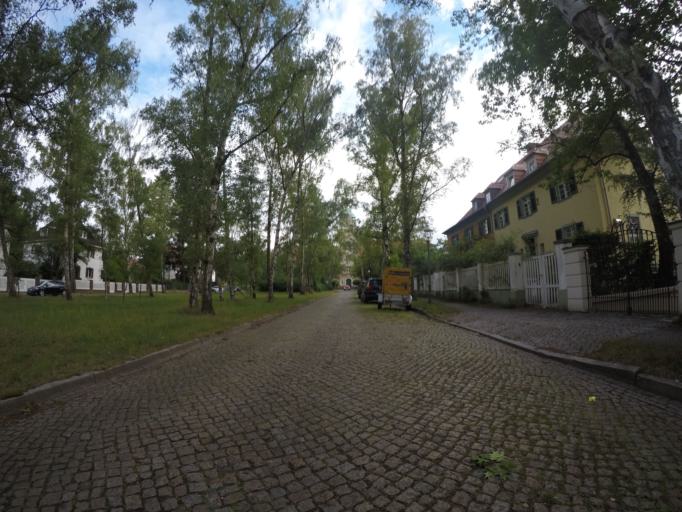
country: DE
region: Berlin
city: Dahlem
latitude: 52.4604
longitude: 13.2808
